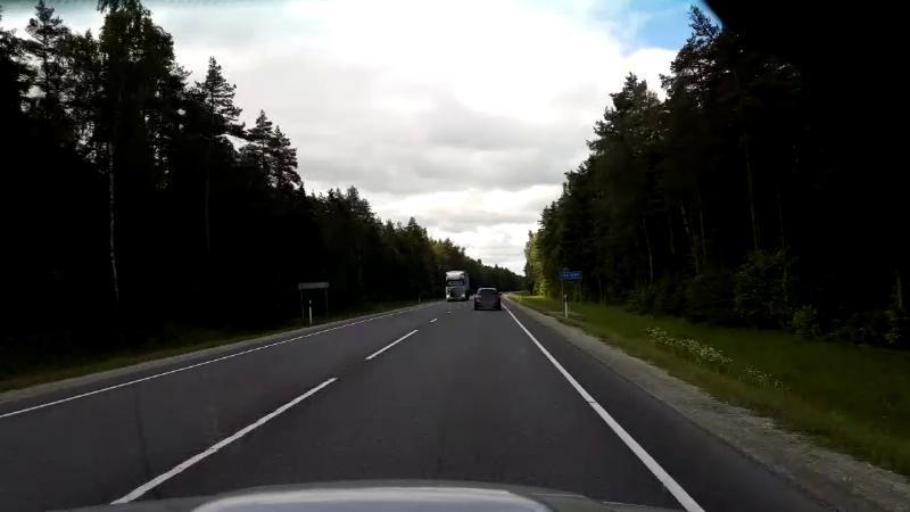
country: EE
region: Raplamaa
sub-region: Maerjamaa vald
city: Marjamaa
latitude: 58.8904
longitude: 24.4539
